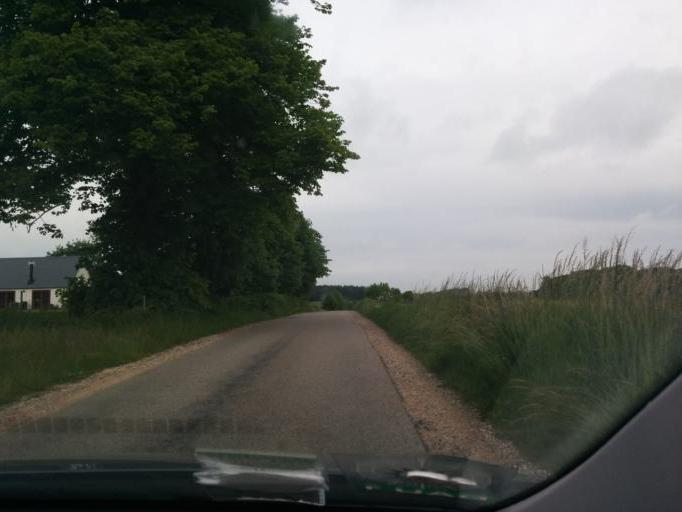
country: DK
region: Central Jutland
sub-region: Syddjurs Kommune
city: Hornslet
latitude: 56.2953
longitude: 10.3829
